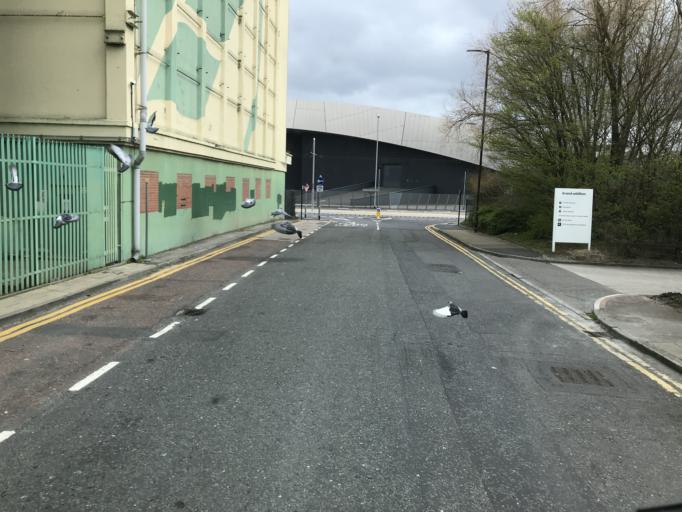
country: GB
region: England
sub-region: Trafford
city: Trafford Park
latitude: 53.4685
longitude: -2.2991
